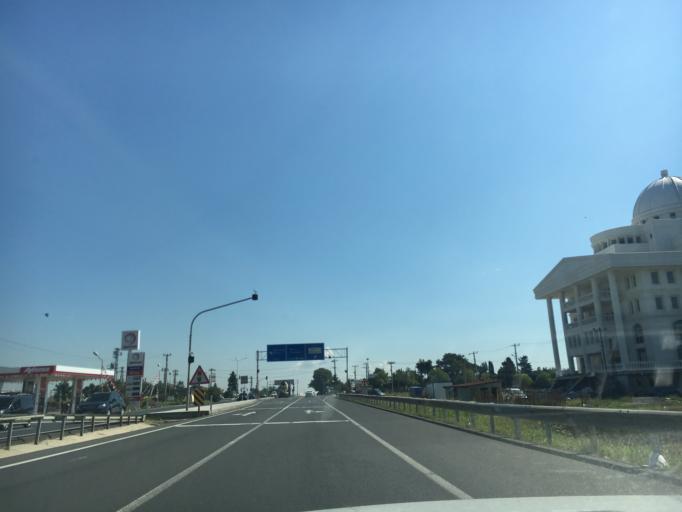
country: TR
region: Tekirdag
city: Marmara Ereglisi
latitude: 40.9764
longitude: 27.9516
